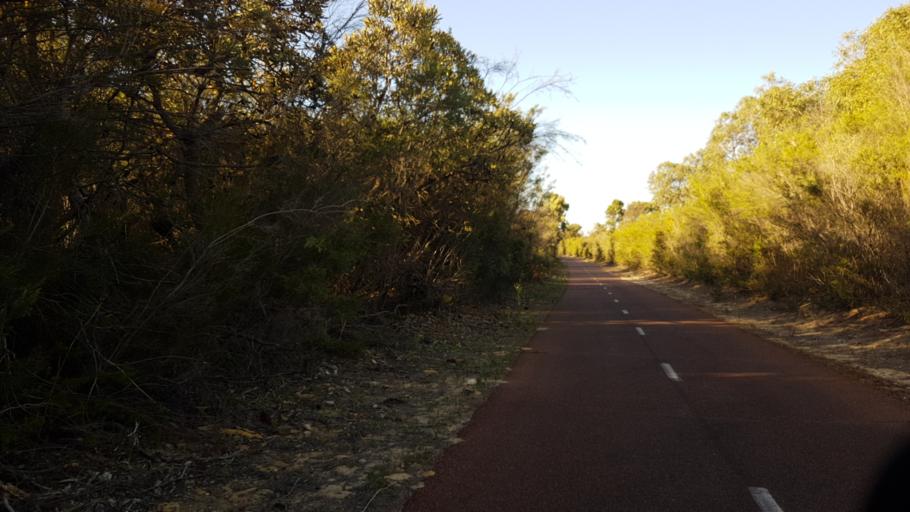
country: AU
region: Western Australia
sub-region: Kwinana
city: Bertram
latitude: -32.2532
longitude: 115.8522
